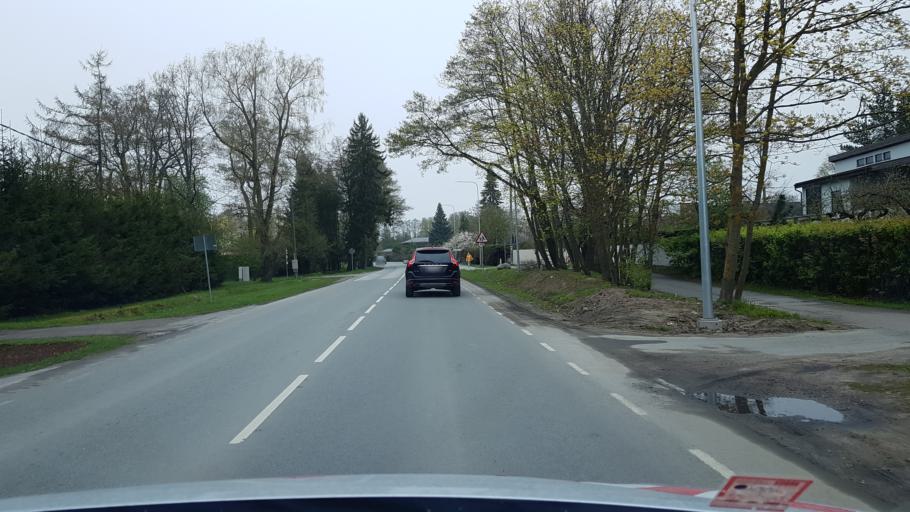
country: EE
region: Harju
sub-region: Viimsi vald
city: Haabneeme
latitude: 59.5132
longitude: 24.8192
